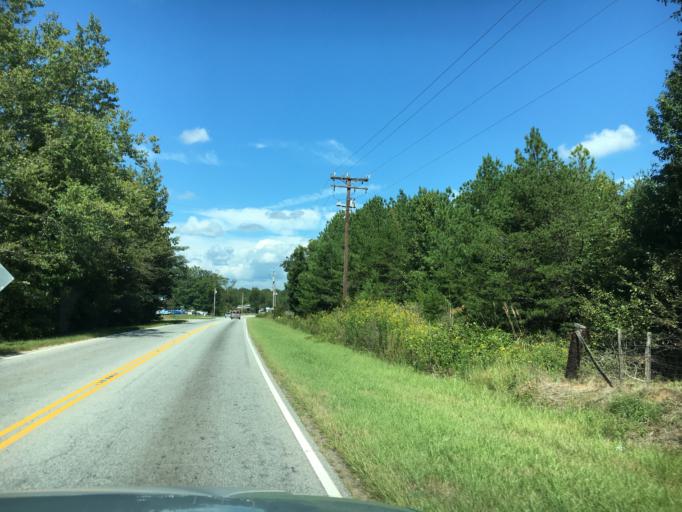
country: US
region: South Carolina
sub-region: Greenville County
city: Taylors
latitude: 34.9733
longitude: -82.3290
